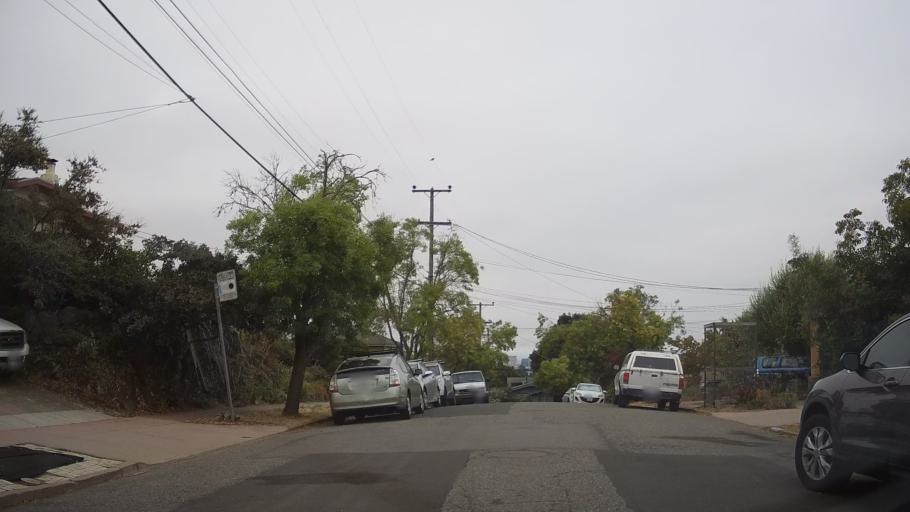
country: US
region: California
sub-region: Alameda County
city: Albany
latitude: 37.8874
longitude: -122.2811
